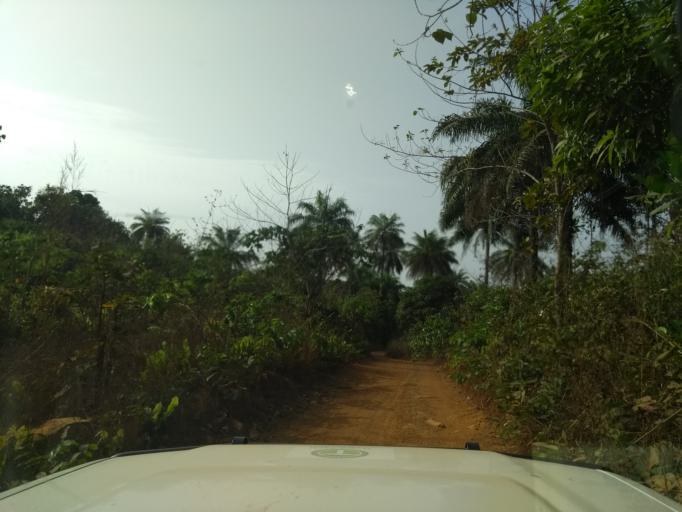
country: GN
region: Kindia
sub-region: Prefecture de Dubreka
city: Dubreka
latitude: 9.8402
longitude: -13.5606
